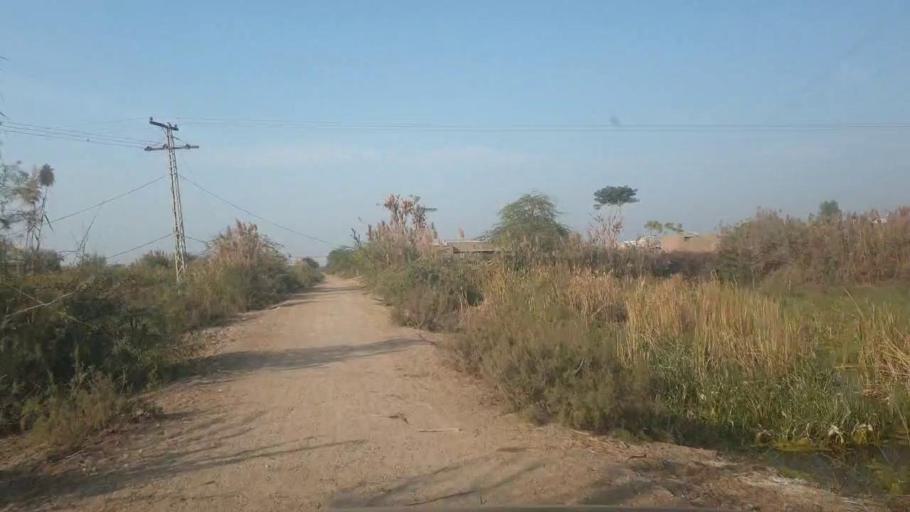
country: PK
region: Sindh
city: Sakrand
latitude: 26.0670
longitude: 68.3454
